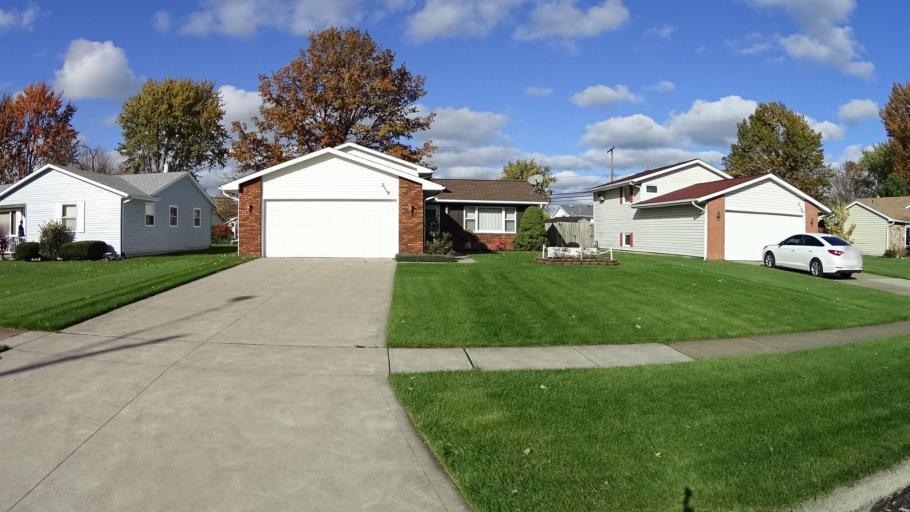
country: US
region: Ohio
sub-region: Lorain County
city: Lorain
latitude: 41.4335
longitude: -82.1999
